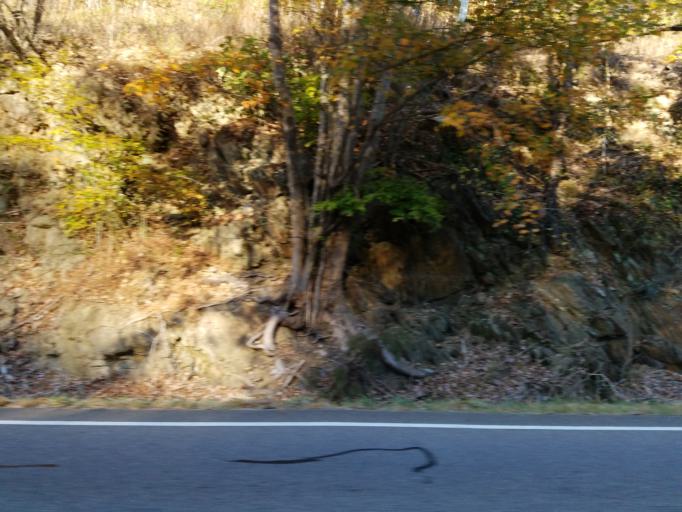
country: US
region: Georgia
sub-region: Gilmer County
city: Ellijay
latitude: 34.6846
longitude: -84.4587
